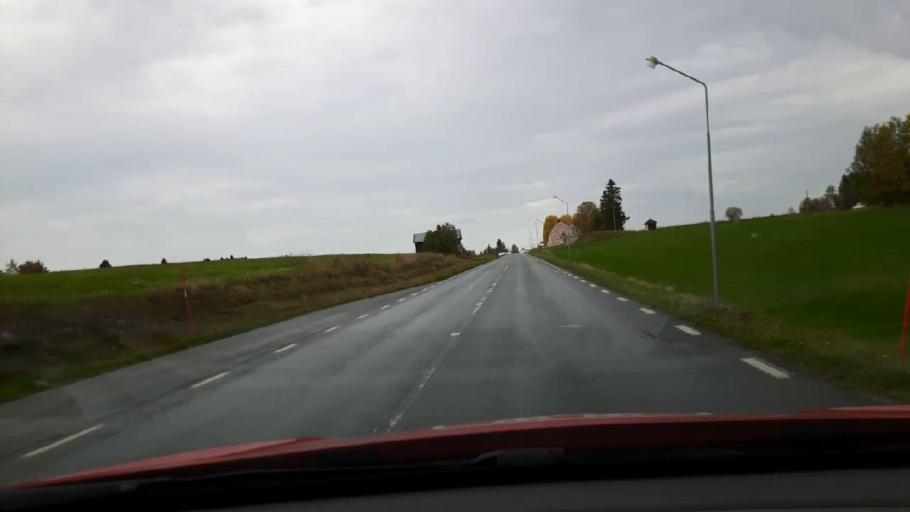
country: SE
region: Jaemtland
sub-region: Bergs Kommun
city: Hoverberg
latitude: 63.0082
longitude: 14.3402
